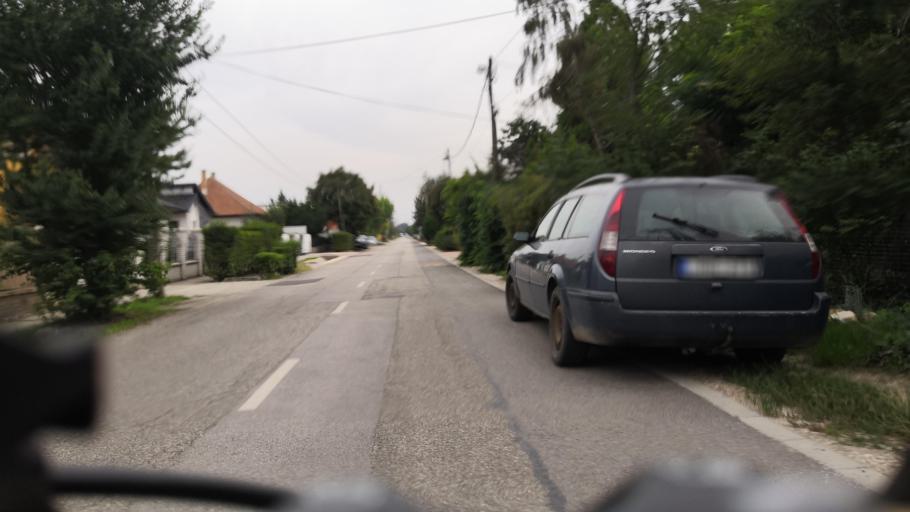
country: HU
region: Csongrad
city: Szeged
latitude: 46.2898
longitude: 20.1634
